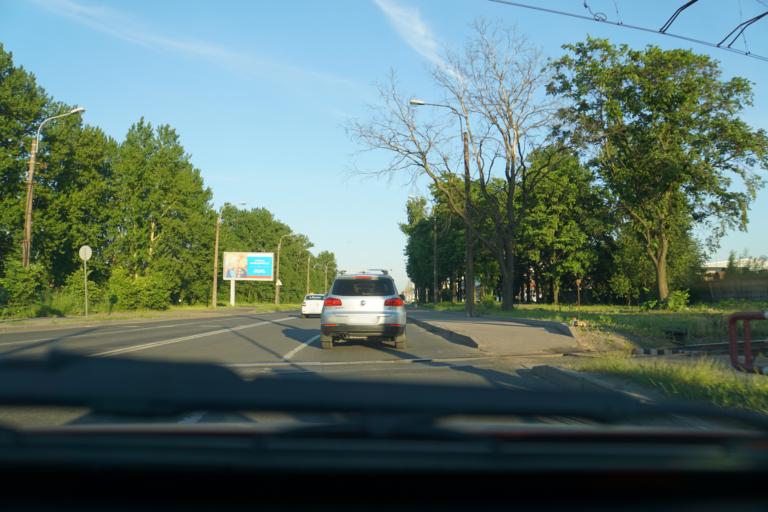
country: RU
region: St.-Petersburg
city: Avtovo
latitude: 59.8615
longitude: 30.2869
